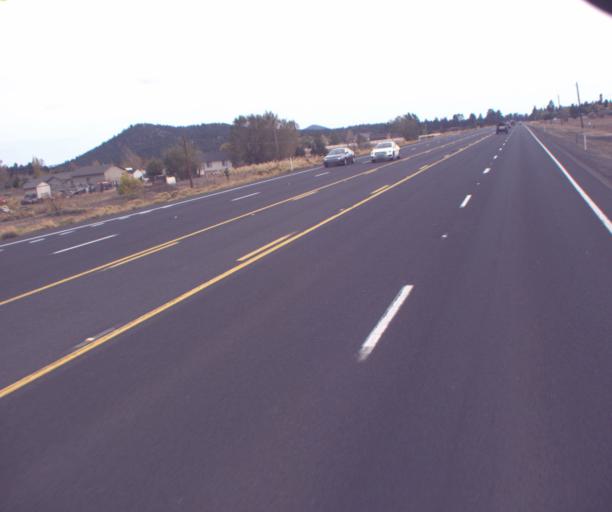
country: US
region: Arizona
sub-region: Coconino County
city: Flagstaff
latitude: 35.2979
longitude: -111.5428
